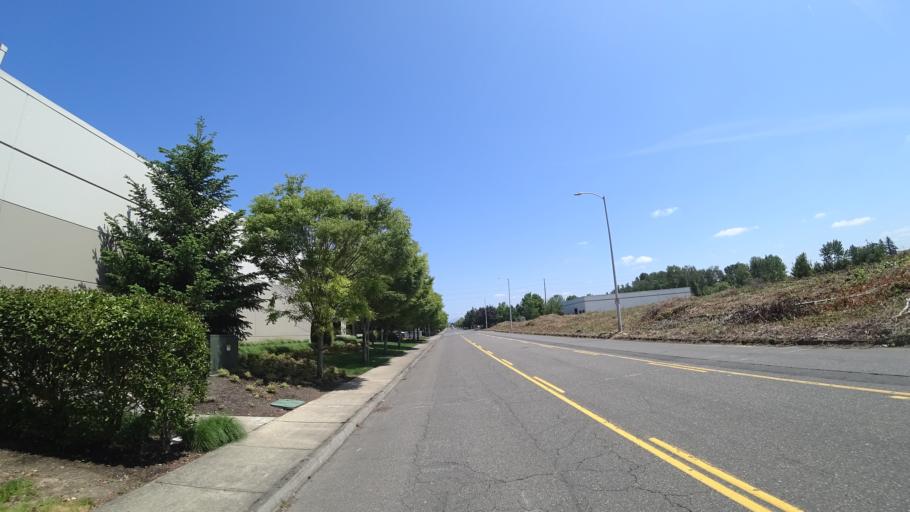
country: US
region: Oregon
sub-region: Multnomah County
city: Fairview
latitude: 45.5528
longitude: -122.4978
